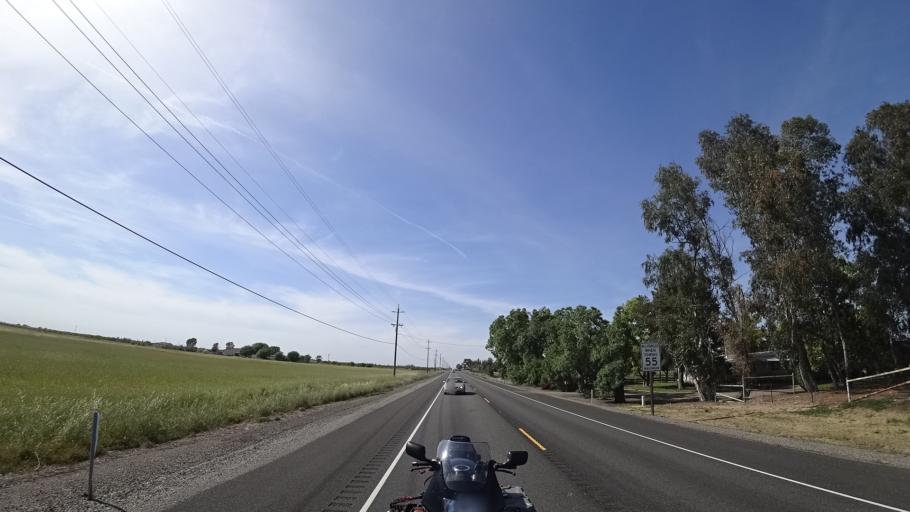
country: US
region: California
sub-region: Glenn County
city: Hamilton City
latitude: 39.8292
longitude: -121.9305
